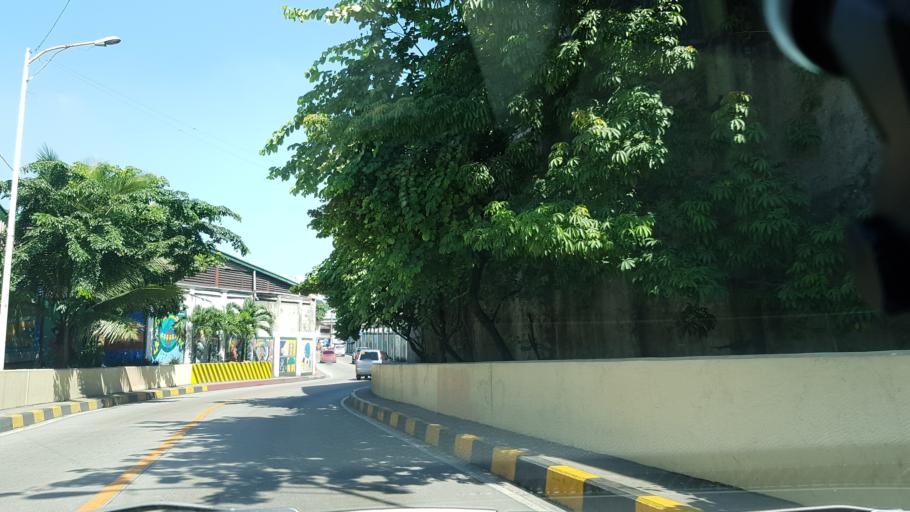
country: PH
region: Calabarzon
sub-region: Province of Rizal
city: Pateros
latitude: 14.5605
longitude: 121.0716
